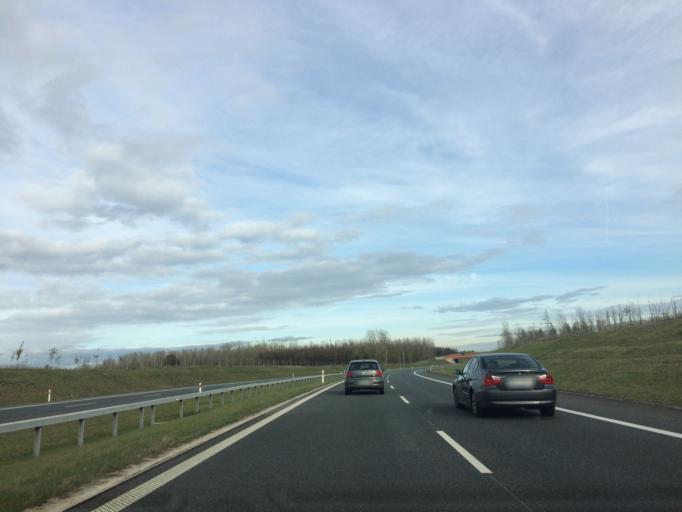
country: PL
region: Lower Silesian Voivodeship
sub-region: Powiat legnicki
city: Milkowice
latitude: 51.1918
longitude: 16.0920
